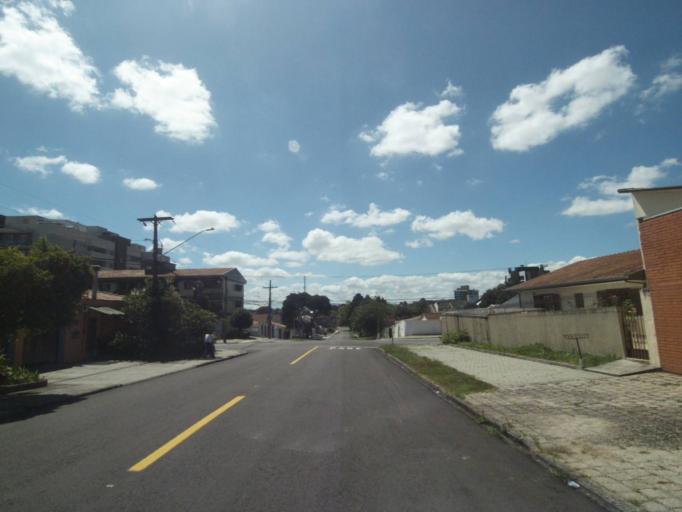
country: BR
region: Parana
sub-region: Pinhais
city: Pinhais
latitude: -25.4403
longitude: -49.2326
